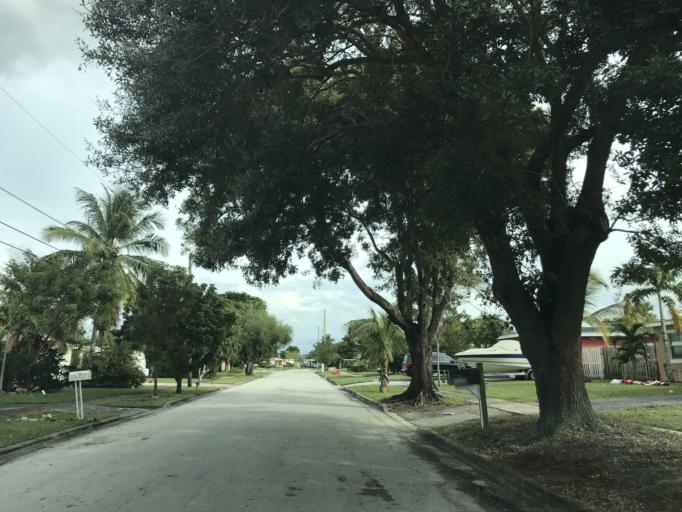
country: US
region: Florida
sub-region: Broward County
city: Margate
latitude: 26.2567
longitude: -80.2117
